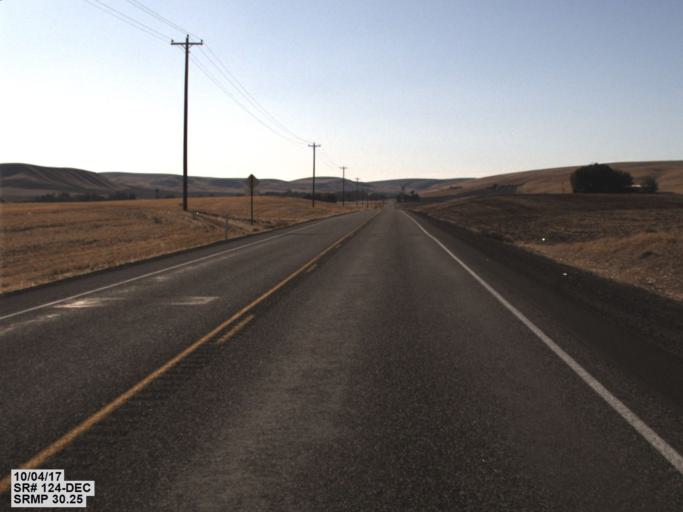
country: US
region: Washington
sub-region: Walla Walla County
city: Garrett
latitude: 46.2987
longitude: -118.4317
